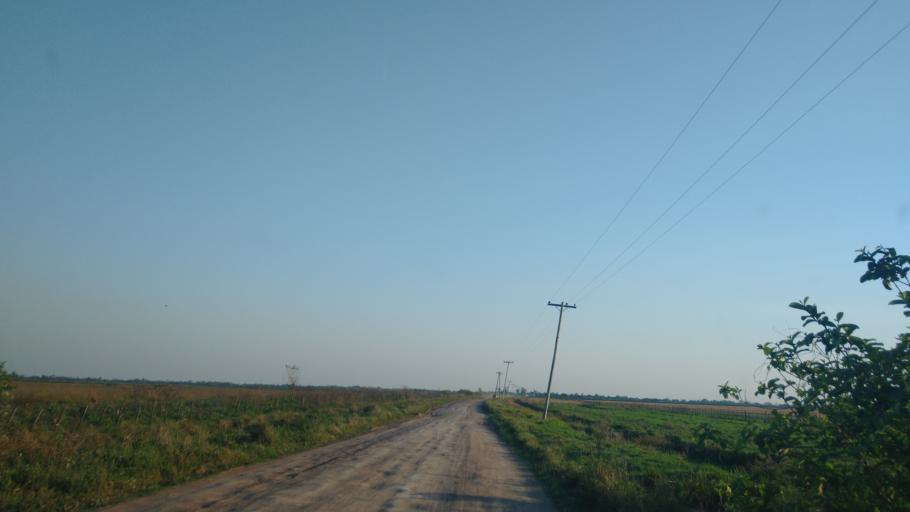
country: PY
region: Neembucu
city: Cerrito
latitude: -27.3908
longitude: -57.6585
